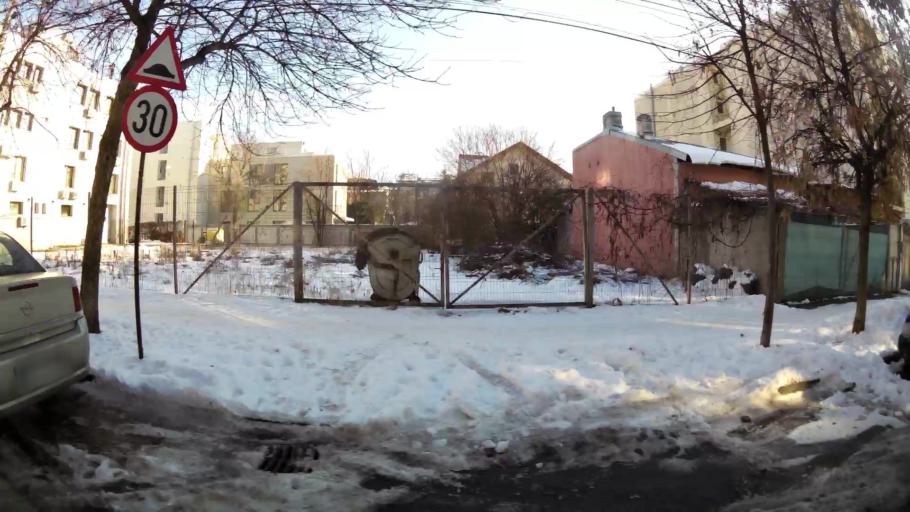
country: RO
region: Bucuresti
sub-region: Municipiul Bucuresti
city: Bucharest
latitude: 44.4820
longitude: 26.0942
